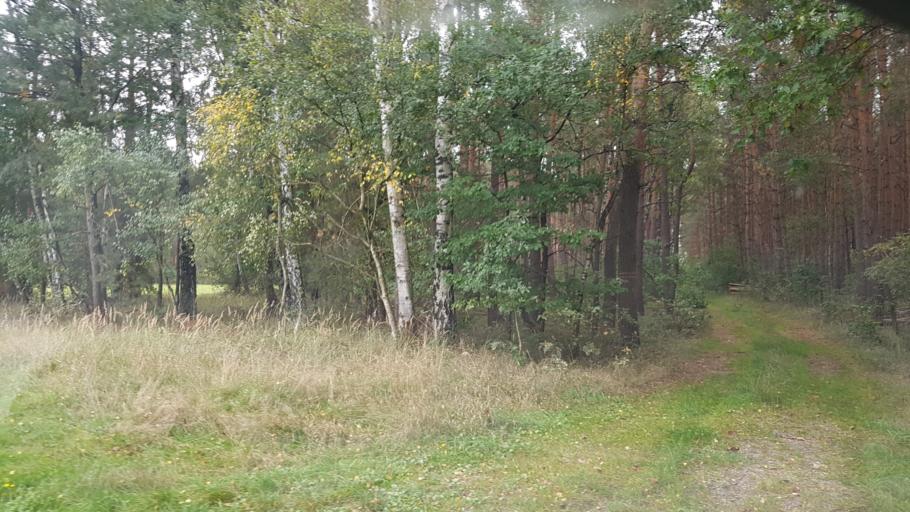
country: DE
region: Brandenburg
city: Finsterwalde
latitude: 51.5809
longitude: 13.6615
